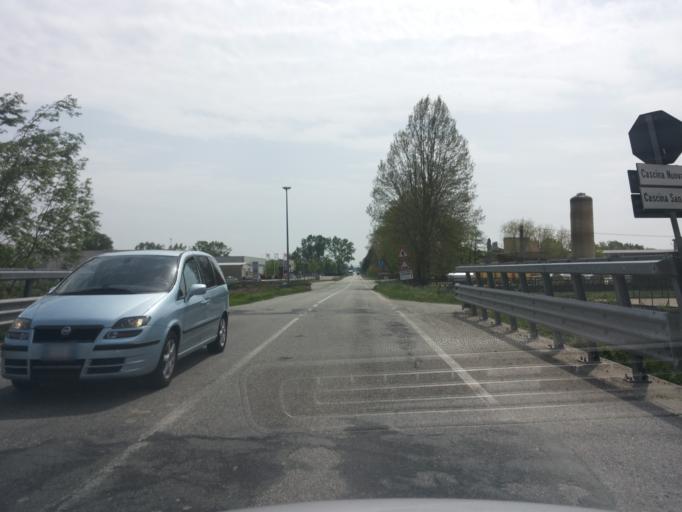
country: IT
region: Piedmont
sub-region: Provincia di Alessandria
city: Occimiano
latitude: 45.0756
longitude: 8.4848
